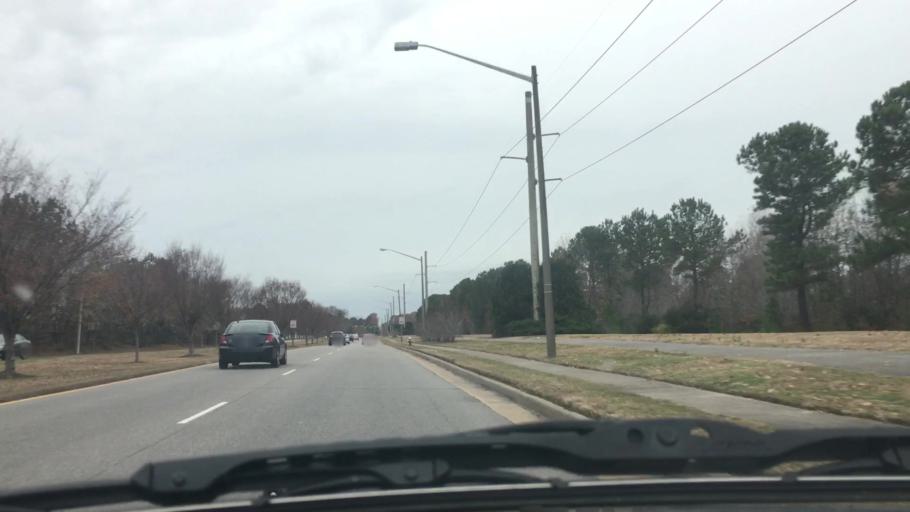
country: US
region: Virginia
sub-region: City of Virginia Beach
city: Virginia Beach
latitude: 36.8098
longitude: -76.1211
